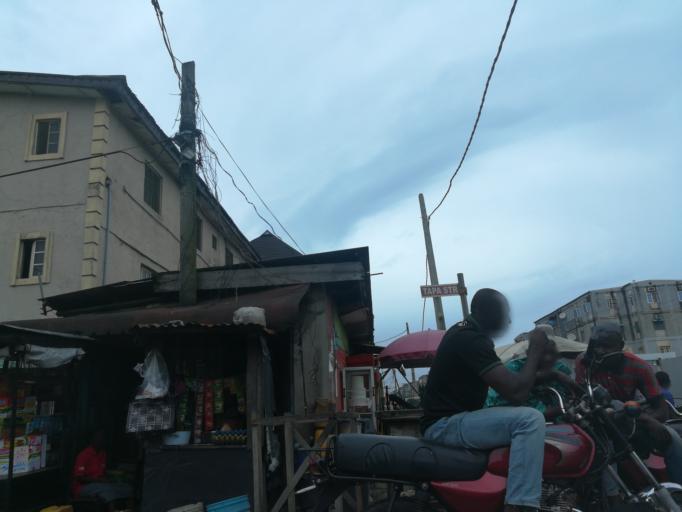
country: NG
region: Lagos
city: Ebute Metta
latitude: 6.4907
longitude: 3.3876
